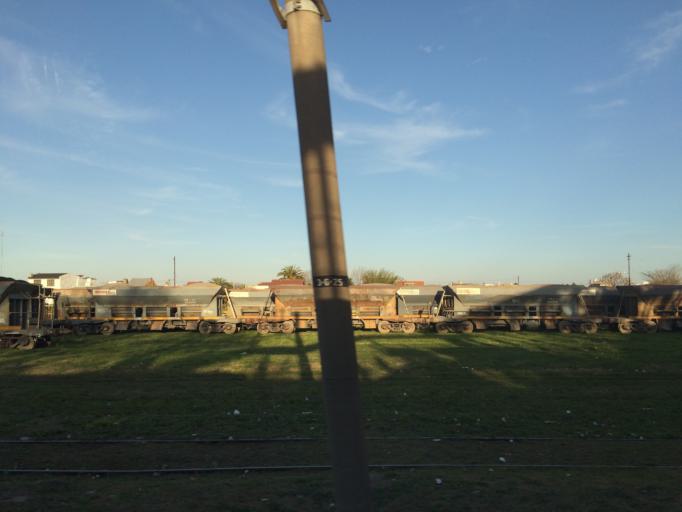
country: AR
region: Buenos Aires
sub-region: Partido de Lanus
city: Lanus
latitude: -34.6869
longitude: -58.3830
